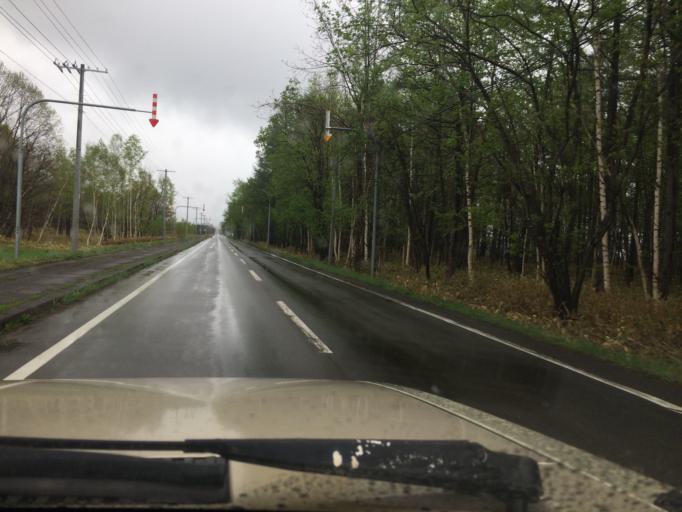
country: JP
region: Hokkaido
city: Obihiro
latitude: 42.8089
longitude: 142.9632
